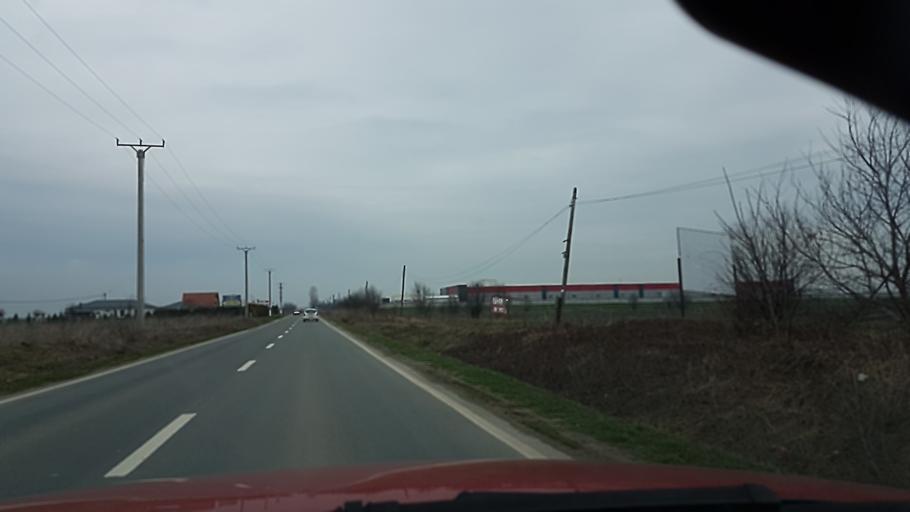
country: RO
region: Ilfov
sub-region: Comuna Balotesti
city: Balotesti
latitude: 44.6167
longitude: 26.1260
